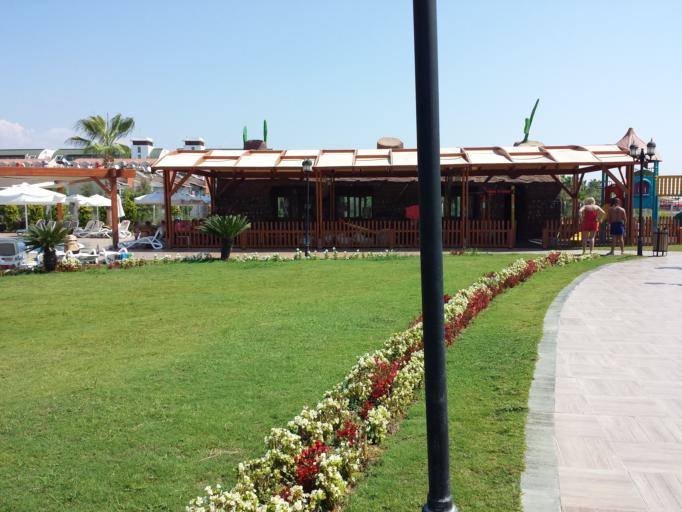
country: TR
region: Antalya
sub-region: Serik
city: Bogazkent
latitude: 36.8319
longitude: 31.1560
